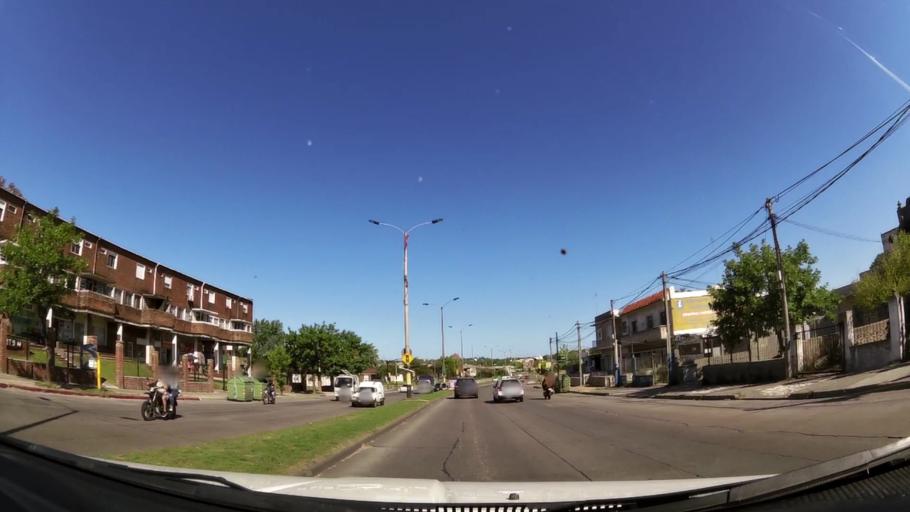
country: UY
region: Montevideo
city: Montevideo
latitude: -34.8439
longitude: -56.1925
